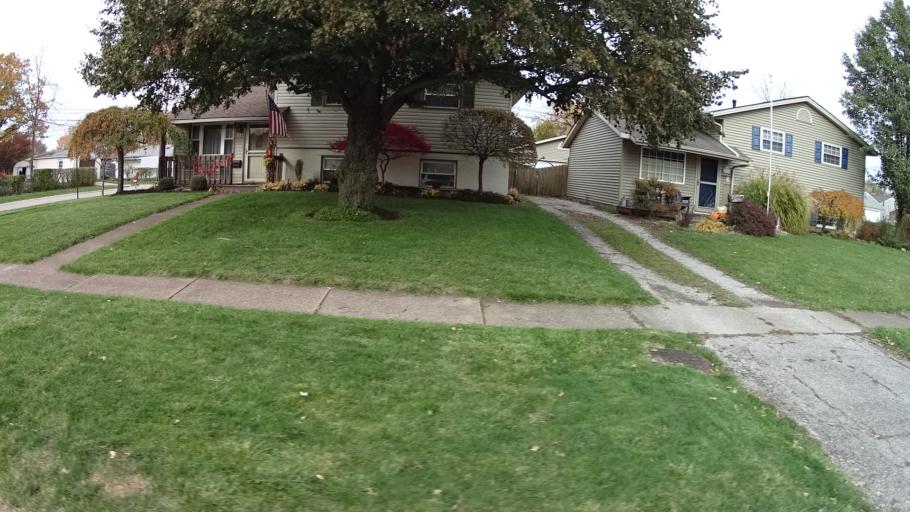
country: US
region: Ohio
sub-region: Lorain County
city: Sheffield Lake
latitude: 41.4794
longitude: -82.1089
